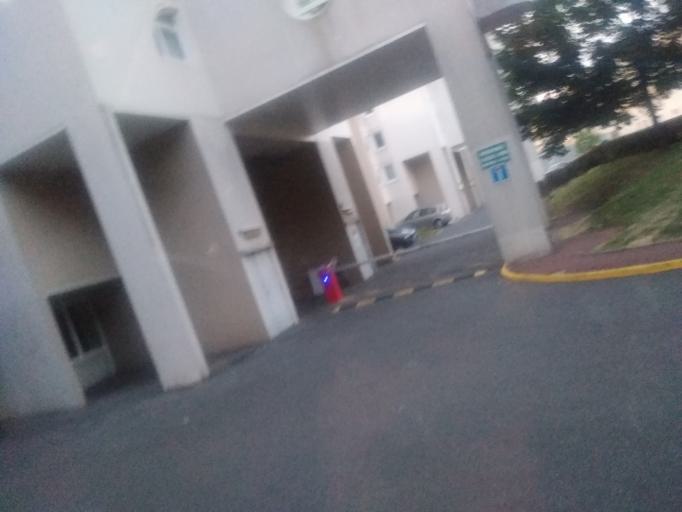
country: FR
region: Ile-de-France
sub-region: Departement de Seine-et-Marne
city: Noisiel
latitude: 48.8413
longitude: 2.6167
